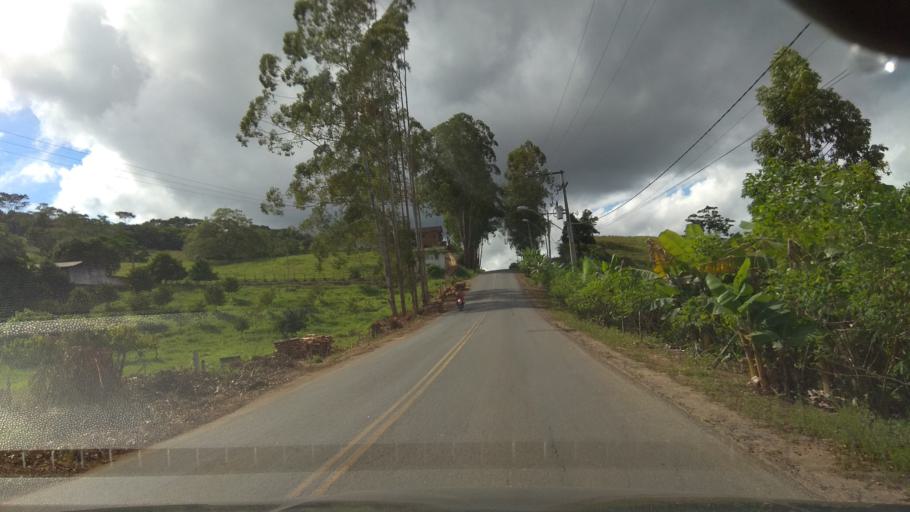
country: BR
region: Bahia
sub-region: Mutuipe
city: Mutuipe
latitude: -13.2551
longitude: -39.5814
